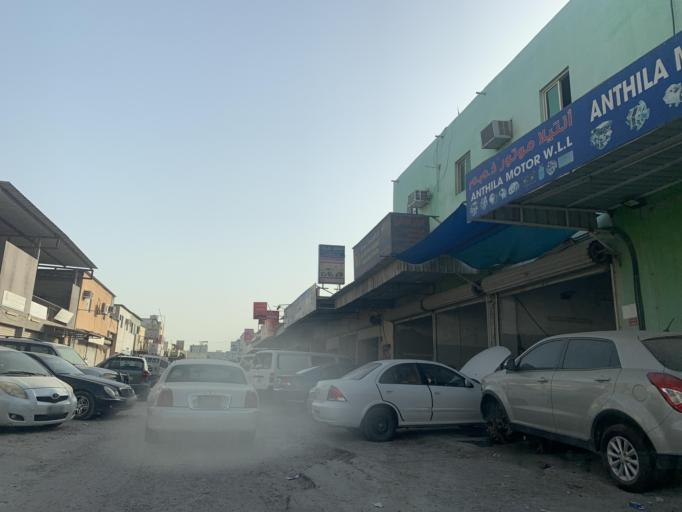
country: BH
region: Central Governorate
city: Madinat Hamad
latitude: 26.1472
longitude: 50.4875
